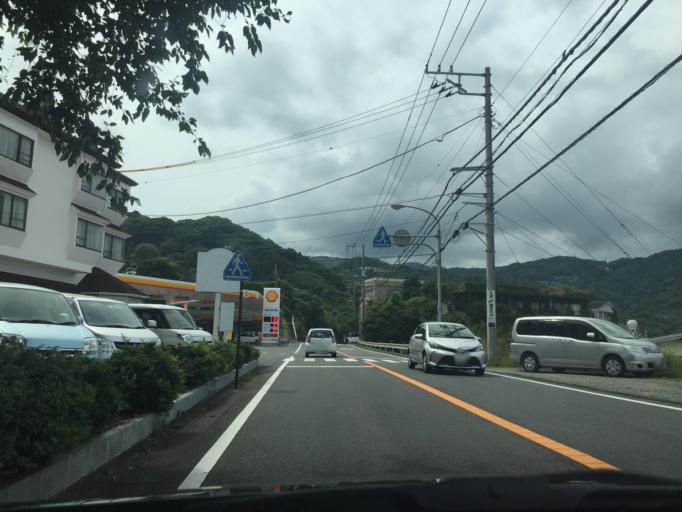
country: JP
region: Shizuoka
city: Shimoda
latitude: 34.7720
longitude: 139.0379
